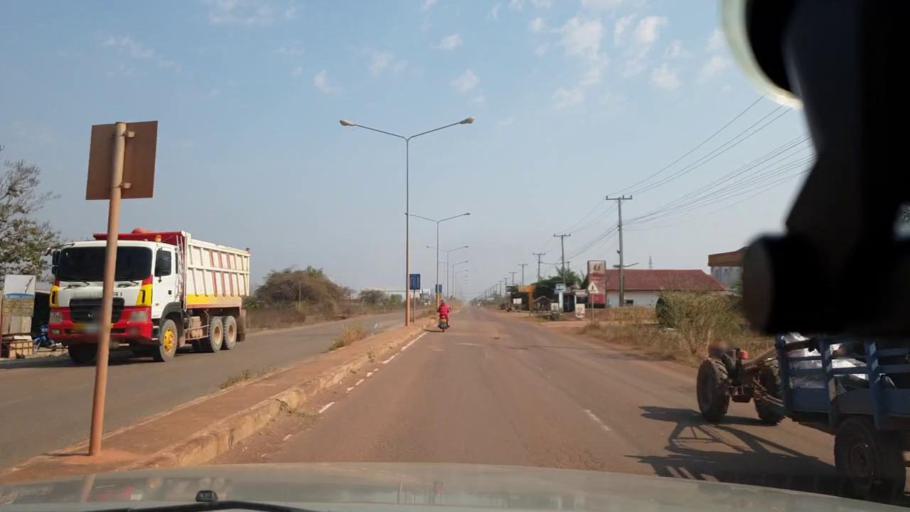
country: LA
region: Vientiane
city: Vientiane
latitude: 18.0048
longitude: 102.7197
